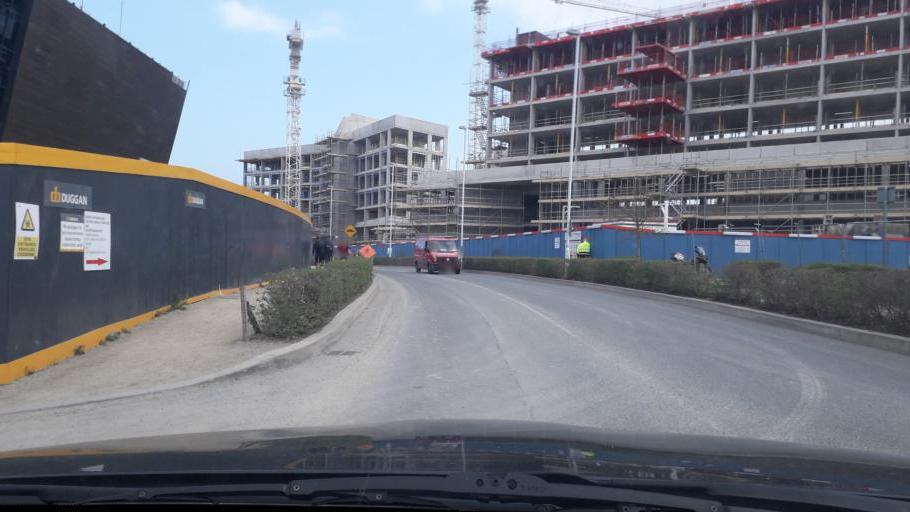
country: IE
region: Leinster
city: Mount Merrion
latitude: 53.3040
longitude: -6.2205
